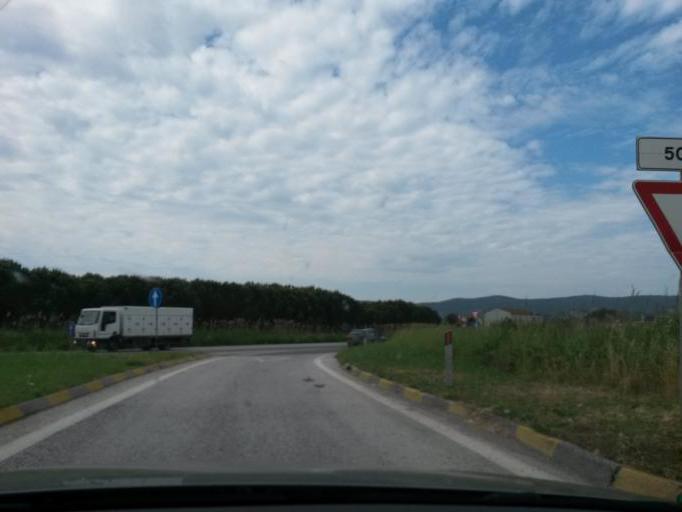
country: IT
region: Tuscany
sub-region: Provincia di Livorno
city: Piombino
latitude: 42.9680
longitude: 10.5540
